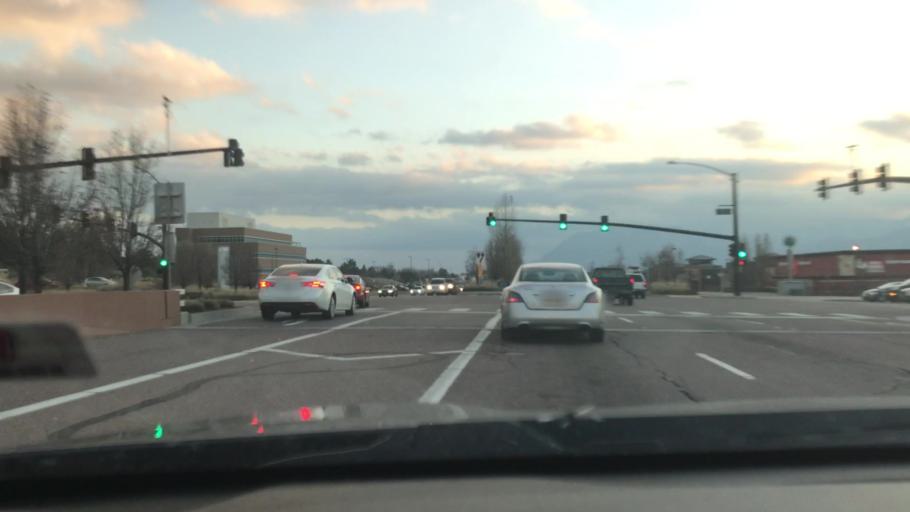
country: US
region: Colorado
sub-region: El Paso County
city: Colorado Springs
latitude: 38.9044
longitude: -104.8172
